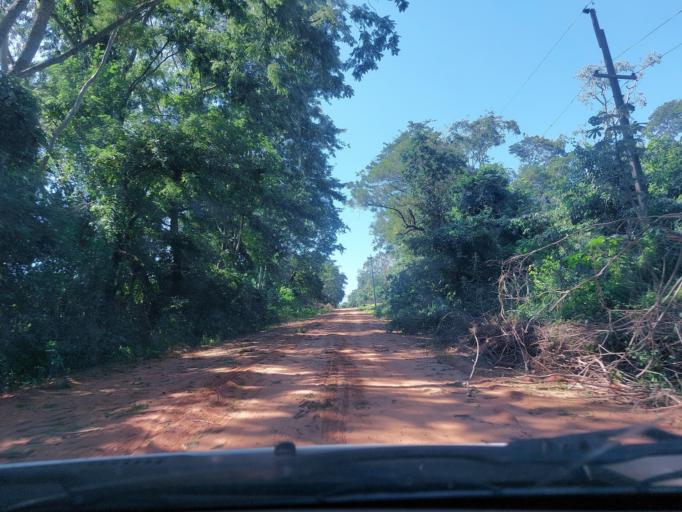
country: PY
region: San Pedro
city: Itacurubi del Rosario
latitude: -24.5405
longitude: -56.5823
